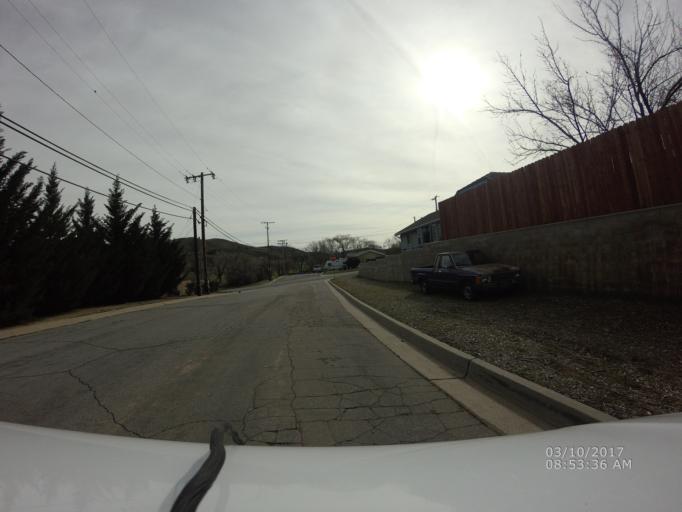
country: US
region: California
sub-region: Los Angeles County
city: Green Valley
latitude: 34.6608
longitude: -118.3870
